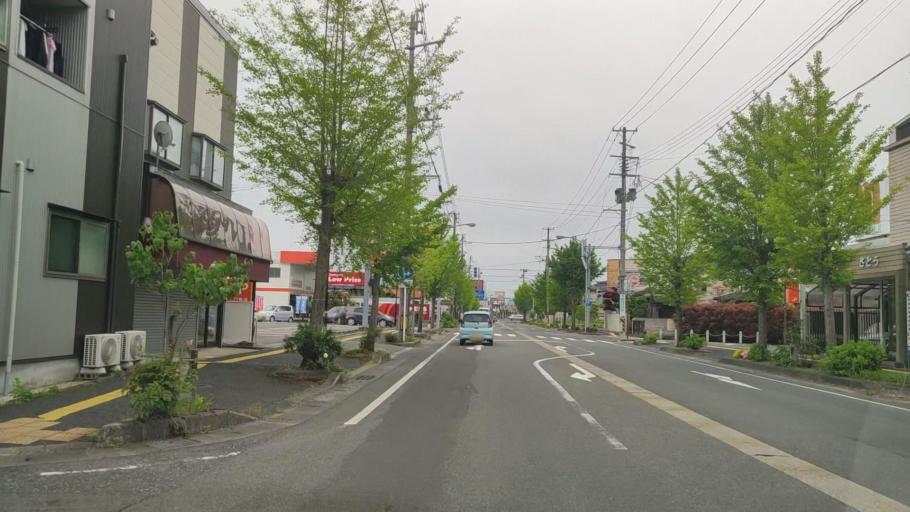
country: JP
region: Niigata
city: Gosen
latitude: 37.7397
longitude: 139.1807
